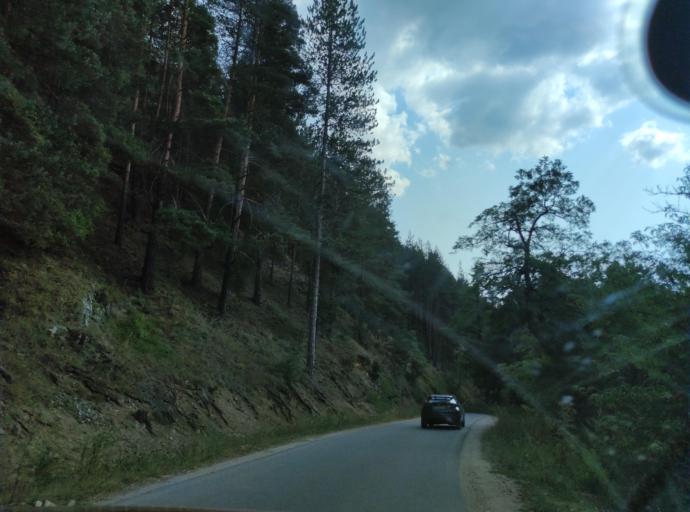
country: BG
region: Blagoevgrad
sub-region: Obshtina Belitsa
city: Belitsa
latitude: 41.9666
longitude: 23.5561
